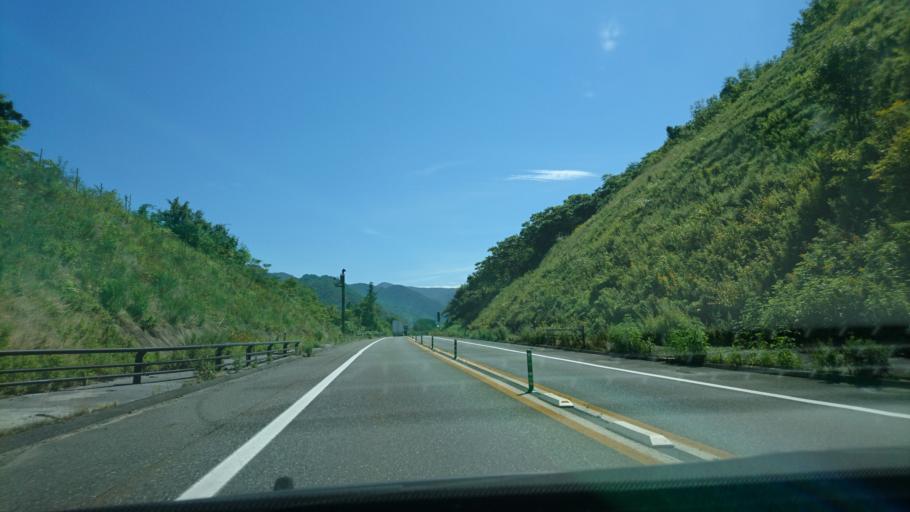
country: JP
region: Iwate
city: Tono
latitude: 39.2631
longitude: 141.6047
